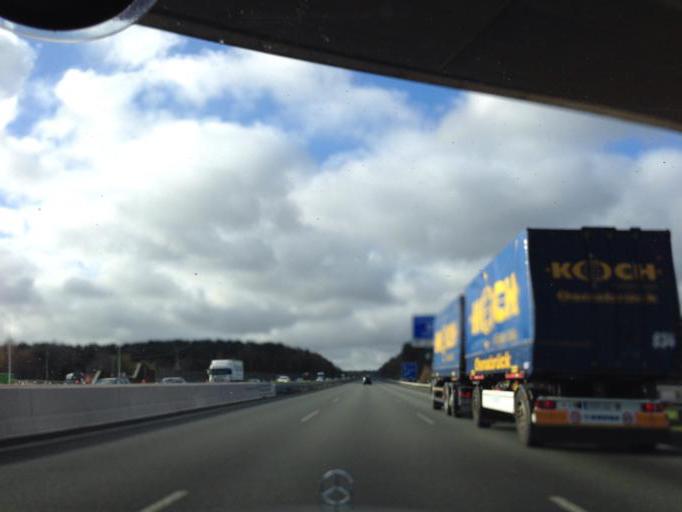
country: DE
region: Lower Saxony
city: Marxen
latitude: 53.3495
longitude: 10.0380
